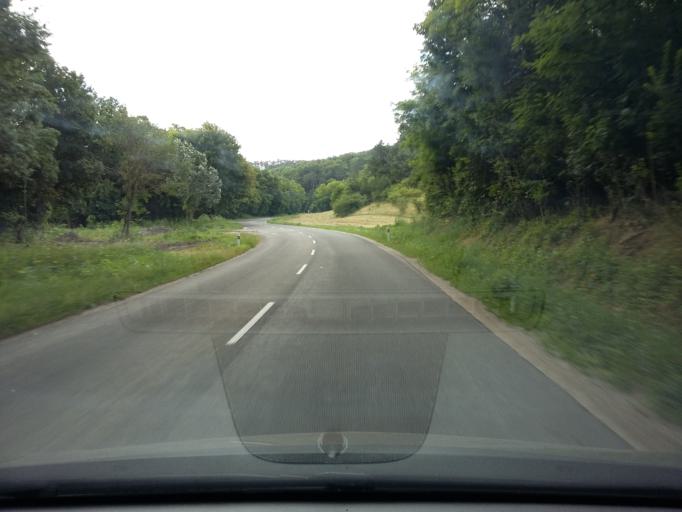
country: SK
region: Trnavsky
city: Smolenice
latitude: 48.5437
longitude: 17.4357
